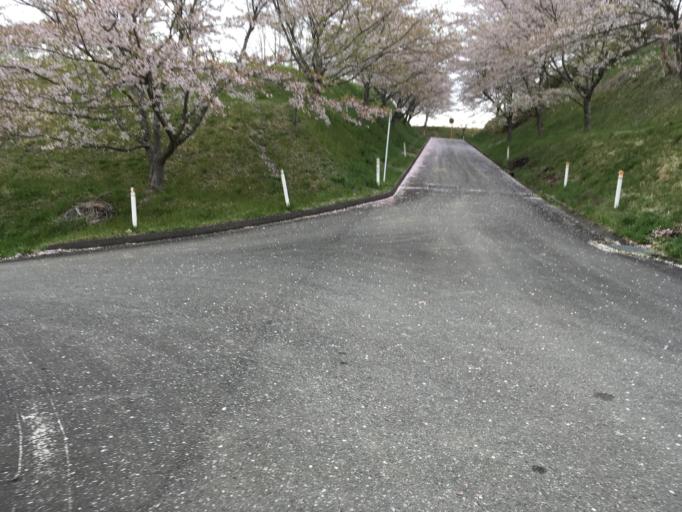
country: JP
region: Iwate
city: Ichinoseki
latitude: 38.8510
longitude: 141.3296
